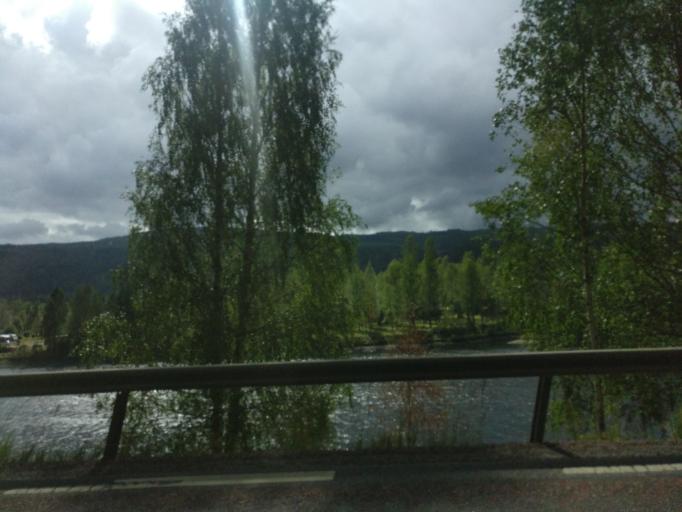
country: SE
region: Vaermland
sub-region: Torsby Kommun
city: Torsby
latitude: 60.7481
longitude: 12.8135
